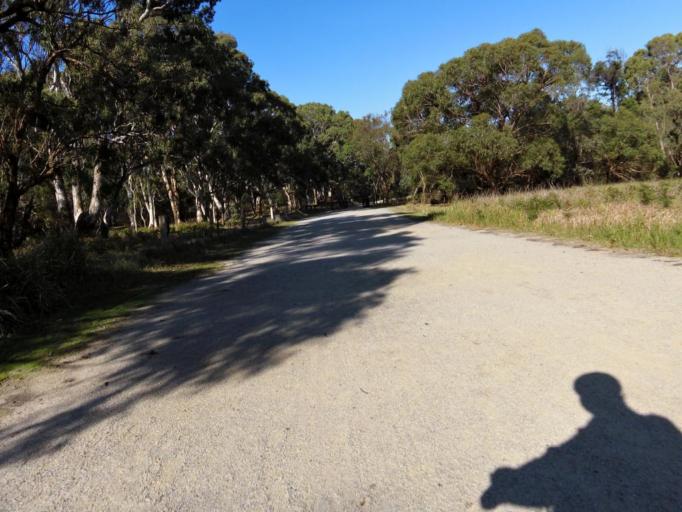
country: AU
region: Victoria
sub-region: Kingston
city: Dingley Village
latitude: -37.9976
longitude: 145.1326
